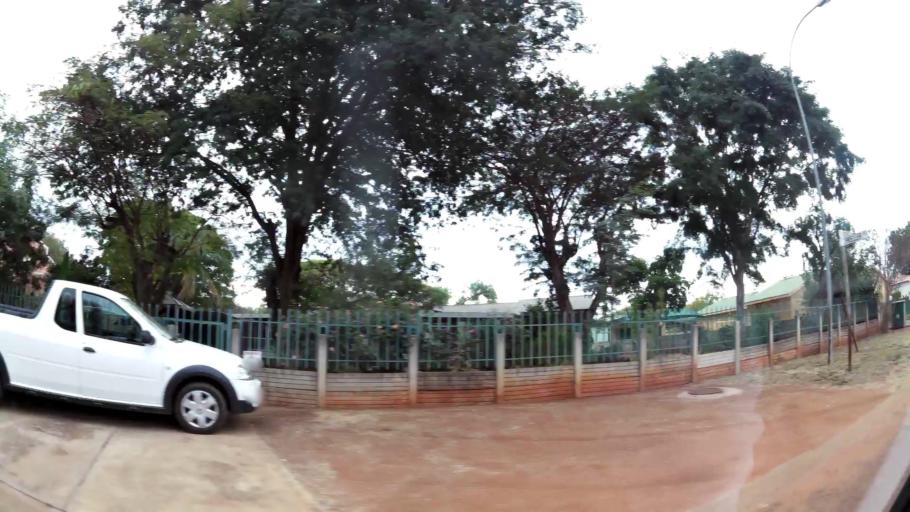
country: ZA
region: Limpopo
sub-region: Waterberg District Municipality
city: Modimolle
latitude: -24.5226
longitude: 28.7049
